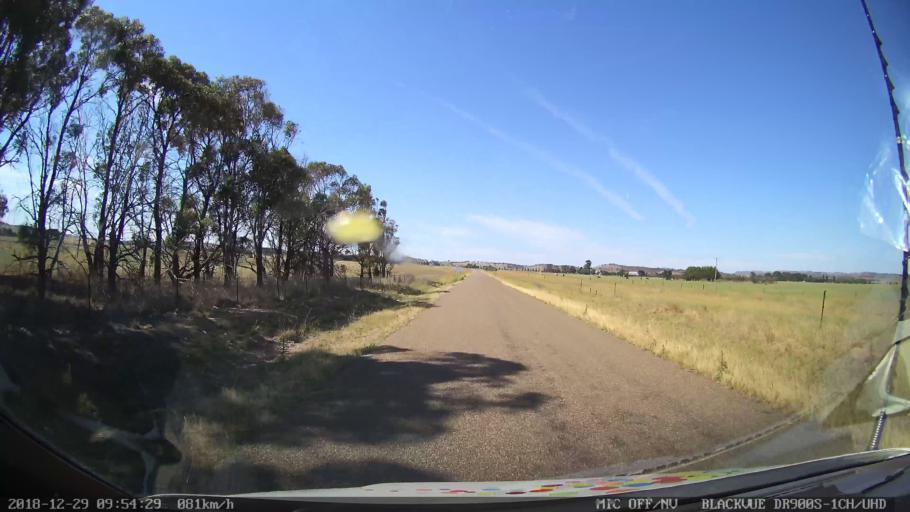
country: AU
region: New South Wales
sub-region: Goulburn Mulwaree
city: Goulburn
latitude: -34.7637
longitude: 149.4669
